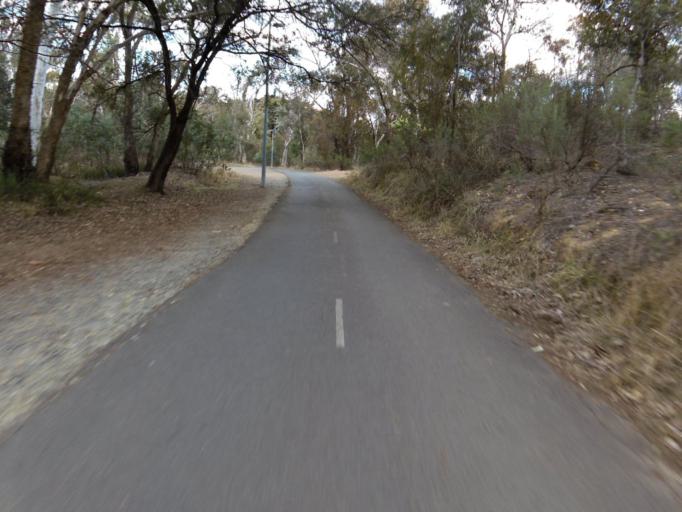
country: AU
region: Australian Capital Territory
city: Acton
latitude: -35.2544
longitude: 149.1089
